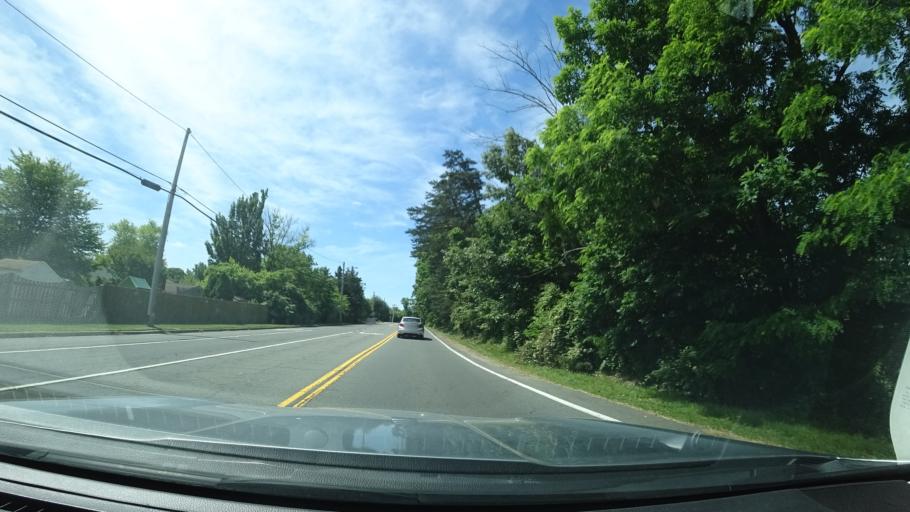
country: US
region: Virginia
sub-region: Loudoun County
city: Oak Grove
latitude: 38.9853
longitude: -77.3972
